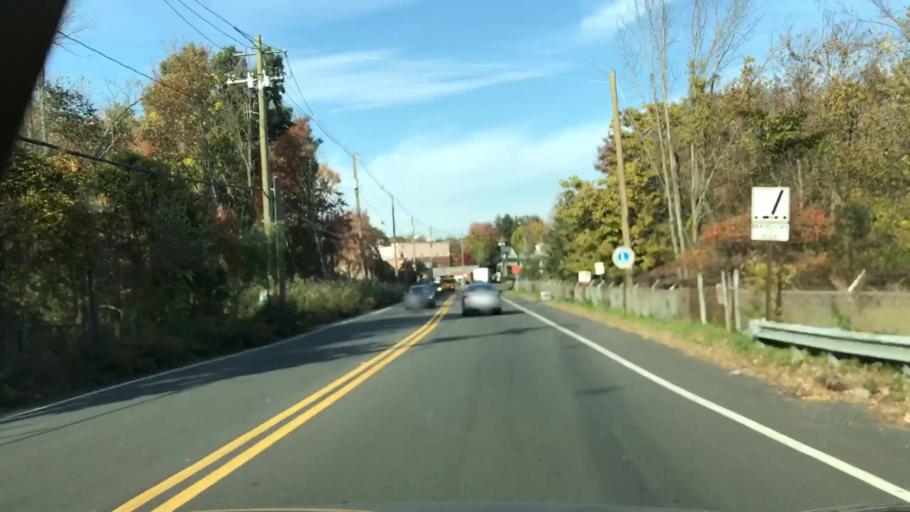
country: US
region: New Jersey
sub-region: Bergen County
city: Harrington Park
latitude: 40.9801
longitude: -73.9789
